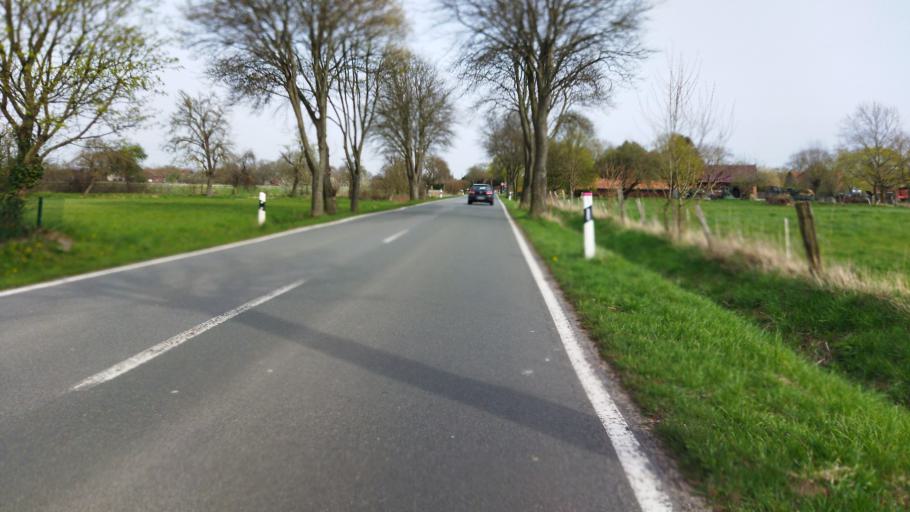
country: DE
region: Lower Saxony
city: Stolzenau
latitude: 52.4837
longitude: 9.0551
